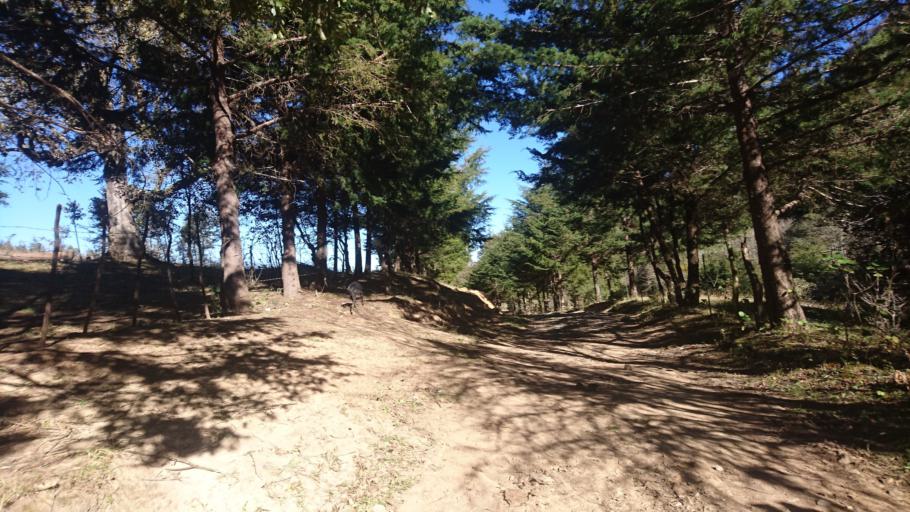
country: MX
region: San Luis Potosi
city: Zaragoza
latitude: 22.0184
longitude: -100.6065
